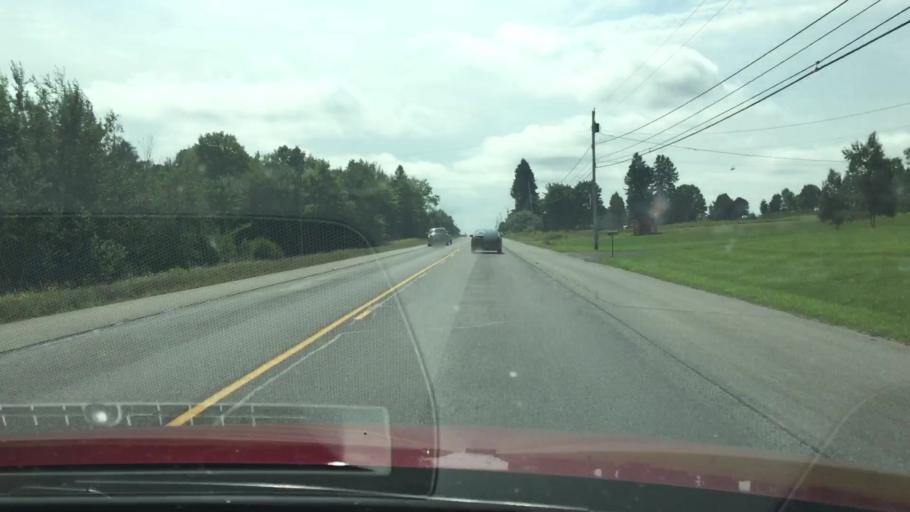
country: US
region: Maine
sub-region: Aroostook County
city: Houlton
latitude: 46.3464
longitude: -67.8420
